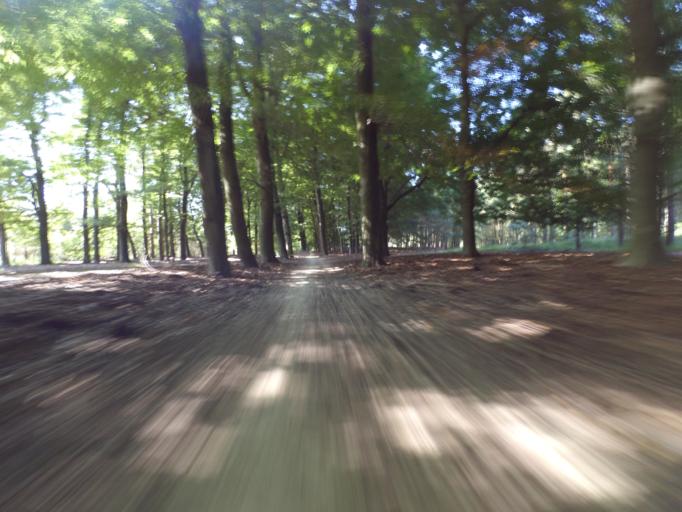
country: NL
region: Gelderland
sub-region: Gemeente Renkum
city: Wolfheze
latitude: 52.0325
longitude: 5.7954
